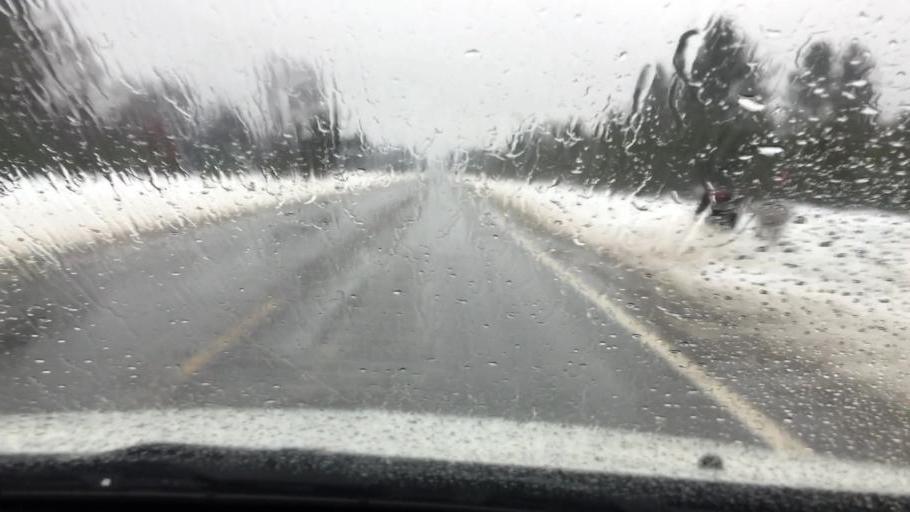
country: US
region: Michigan
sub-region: Charlevoix County
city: East Jordan
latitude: 45.0450
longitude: -85.0693
